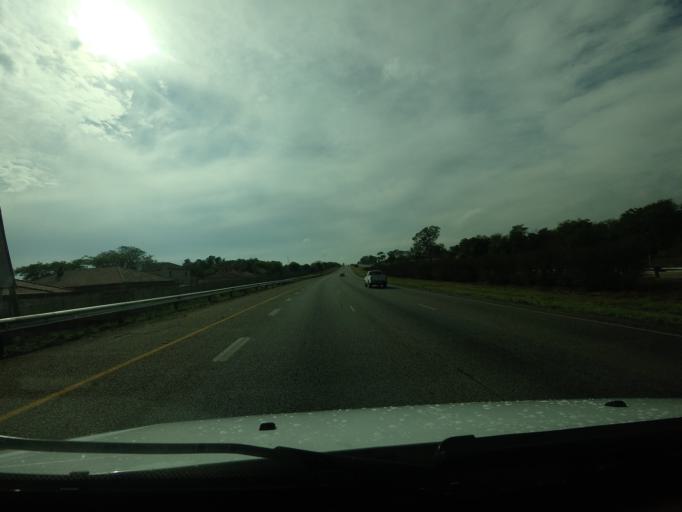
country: ZA
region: Gauteng
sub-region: City of Tshwane Metropolitan Municipality
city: Pretoria
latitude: -25.7523
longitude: 28.3350
